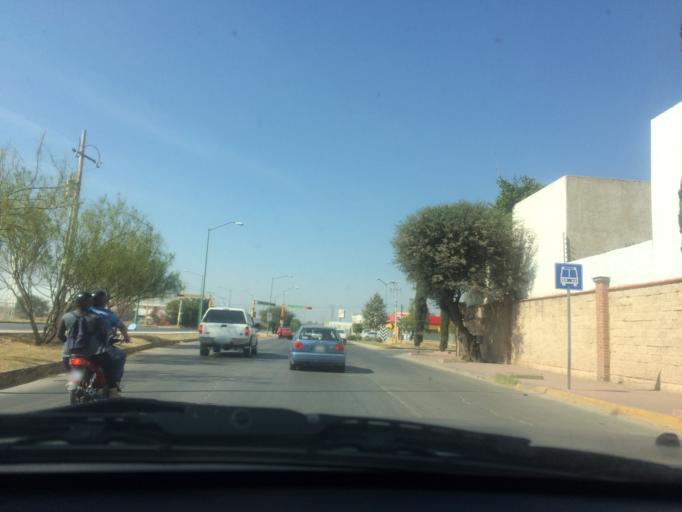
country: MX
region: Guanajuato
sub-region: Leon
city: Medina
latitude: 21.1251
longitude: -101.6220
